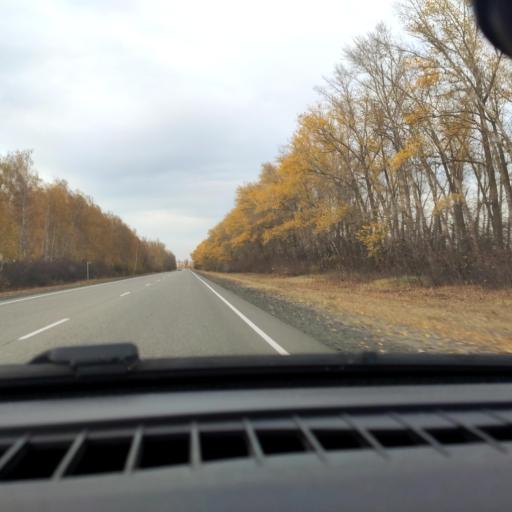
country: RU
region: Voronezj
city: Ostrogozhsk
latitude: 50.9942
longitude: 38.9991
